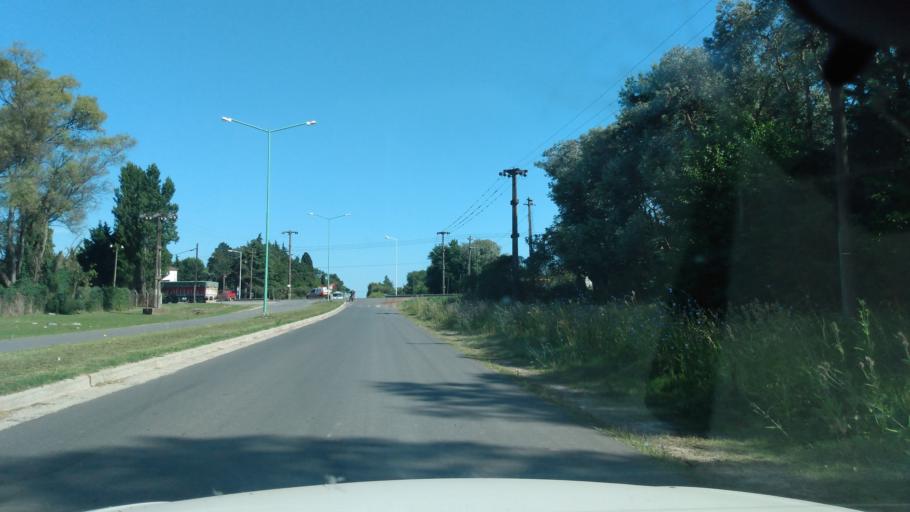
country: AR
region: Buenos Aires
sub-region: Partido de Lujan
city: Lujan
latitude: -34.5502
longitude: -59.1357
